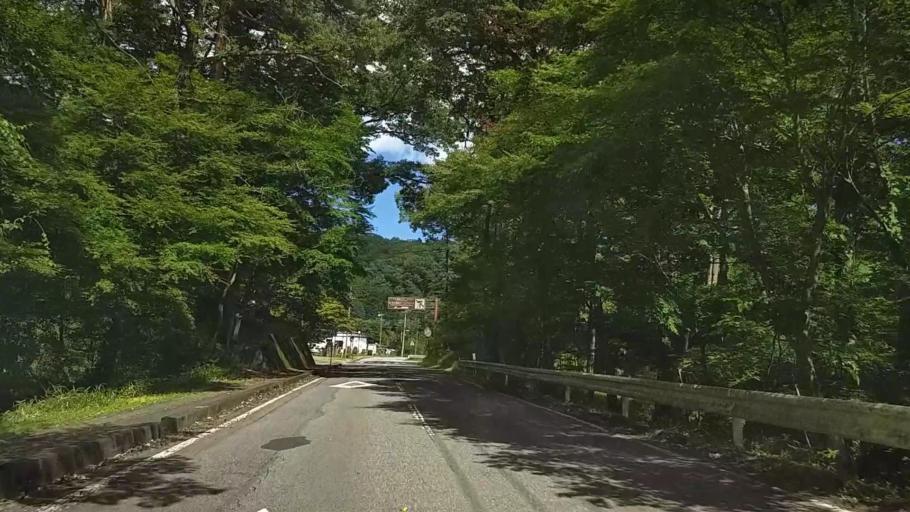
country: JP
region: Tochigi
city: Nikko
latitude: 36.7564
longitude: 139.6131
